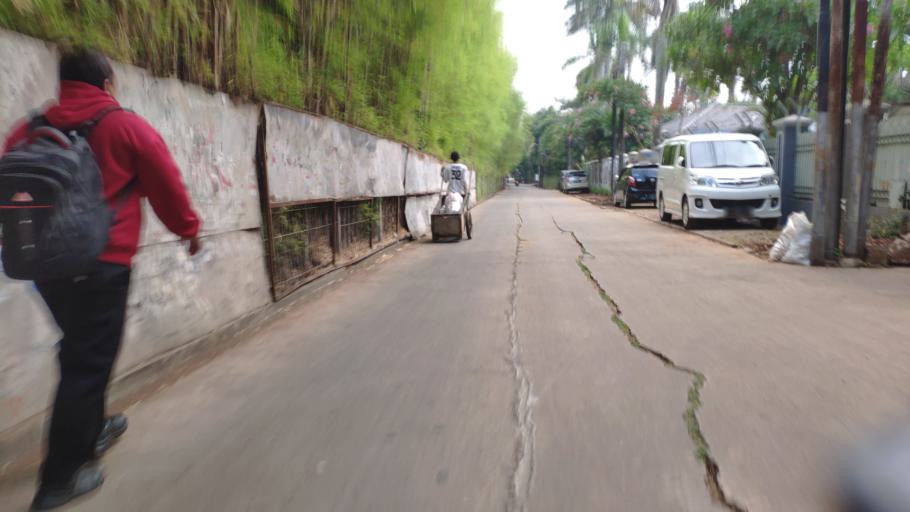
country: ID
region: Jakarta Raya
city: Jakarta
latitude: -6.2931
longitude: 106.8124
